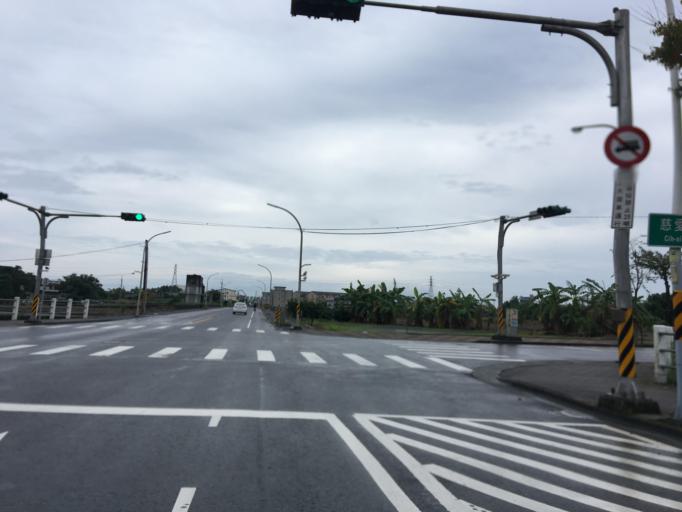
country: TW
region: Taiwan
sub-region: Yilan
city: Yilan
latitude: 24.6366
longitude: 121.7958
